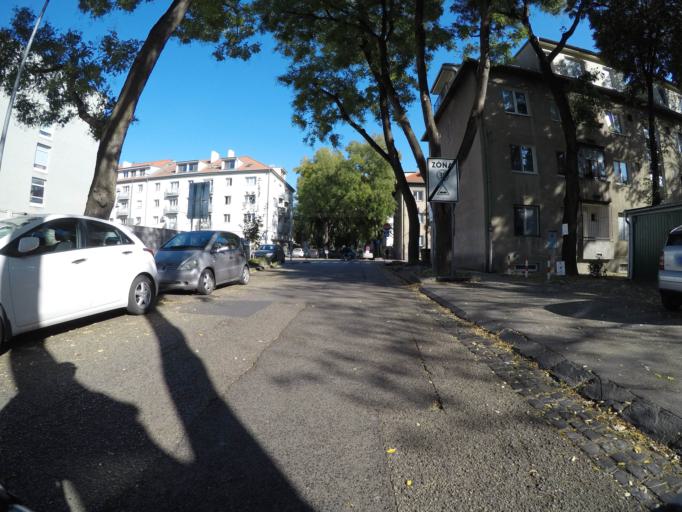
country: SK
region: Bratislavsky
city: Bratislava
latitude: 48.1511
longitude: 17.1292
